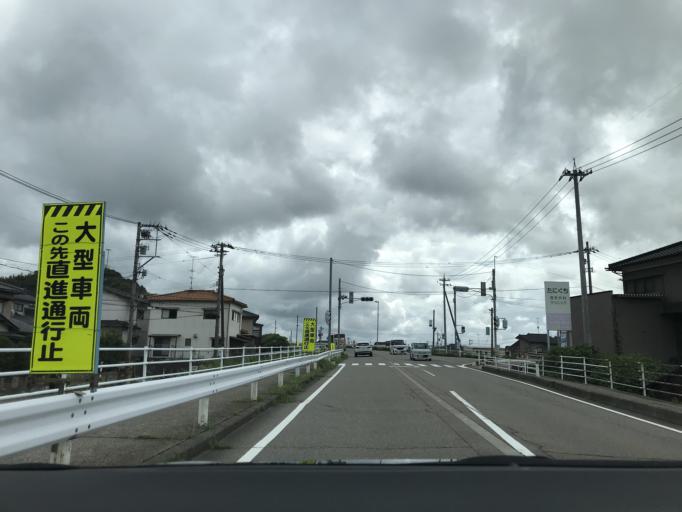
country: JP
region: Ishikawa
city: Tsubata
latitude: 36.6555
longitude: 136.7276
